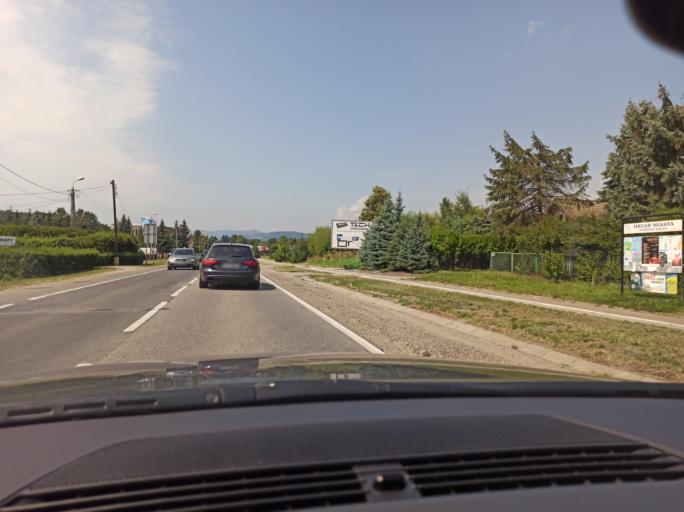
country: PL
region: Lesser Poland Voivodeship
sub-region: Powiat nowosadecki
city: Nowy Sacz
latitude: 49.6225
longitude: 20.7390
